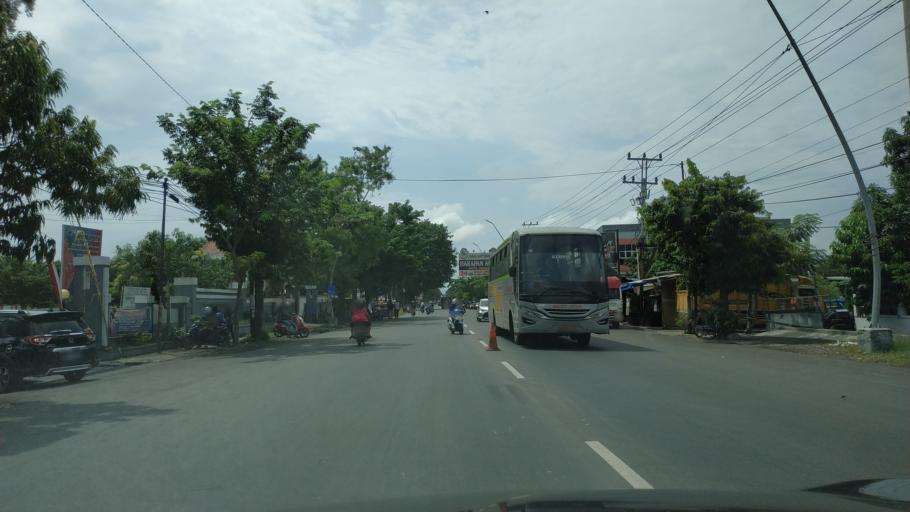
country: ID
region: Central Java
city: Tegal
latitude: -6.8772
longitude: 109.1271
